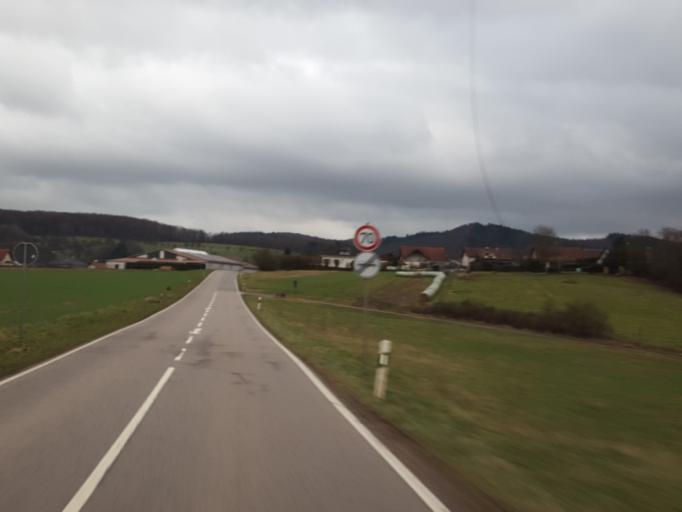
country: DE
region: Saarland
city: Nalbach
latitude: 49.4210
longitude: 6.7586
